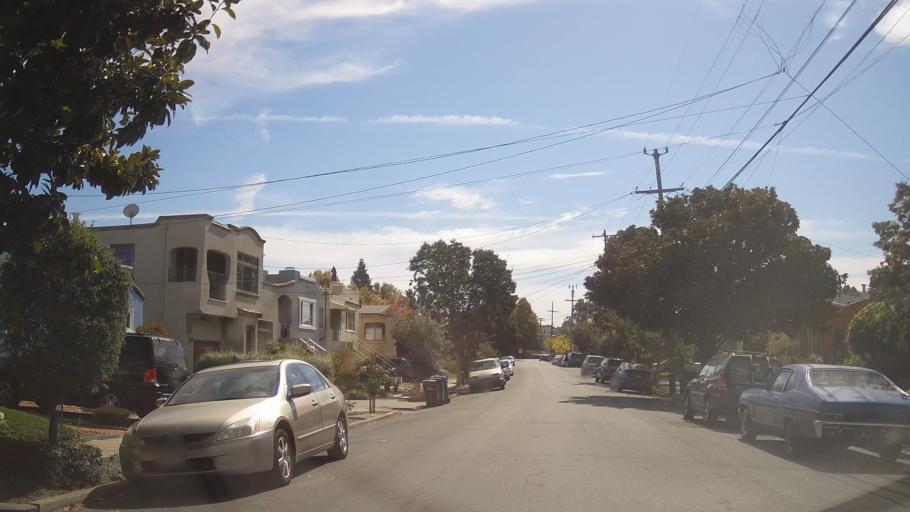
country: US
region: California
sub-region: Alameda County
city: Albany
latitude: 37.8861
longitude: -122.2904
